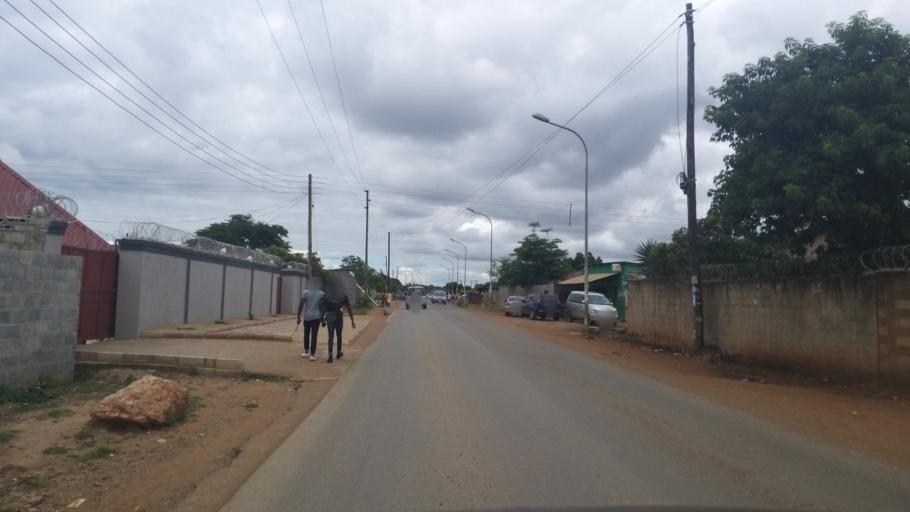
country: ZM
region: Lusaka
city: Lusaka
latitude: -15.4446
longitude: 28.3063
